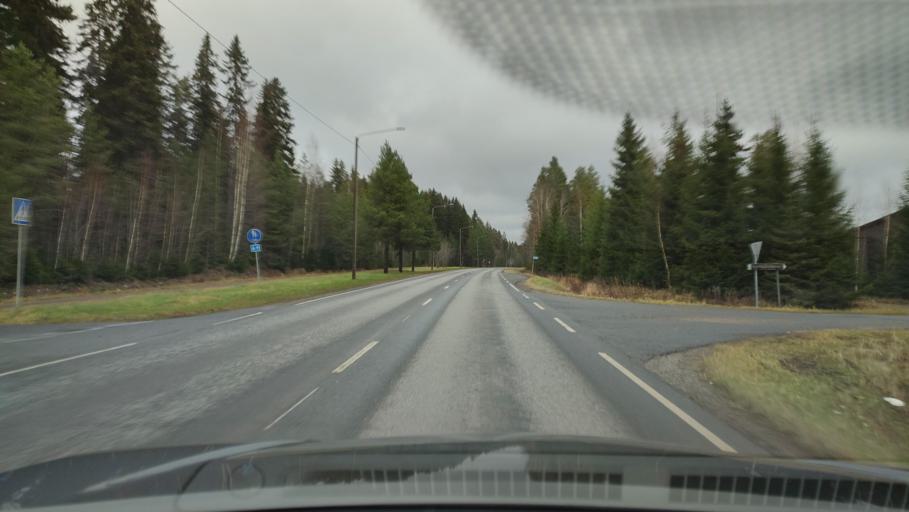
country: FI
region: Southern Ostrobothnia
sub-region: Suupohja
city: Kauhajoki
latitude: 62.4013
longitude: 22.1594
